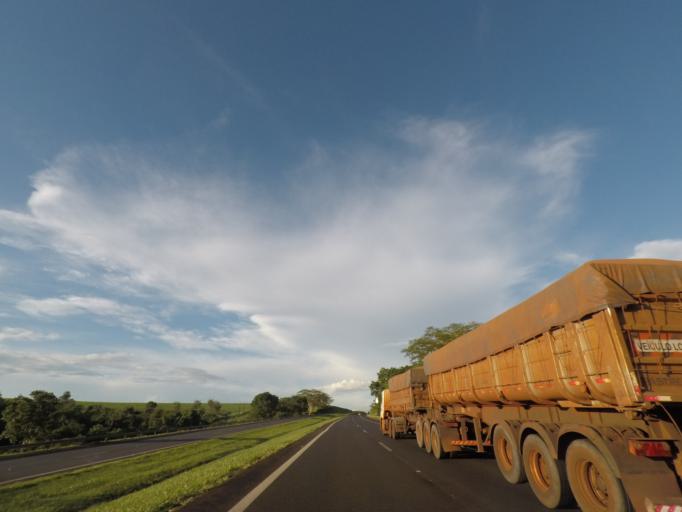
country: BR
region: Sao Paulo
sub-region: Ituverava
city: Ituverava
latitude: -20.2543
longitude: -47.7997
